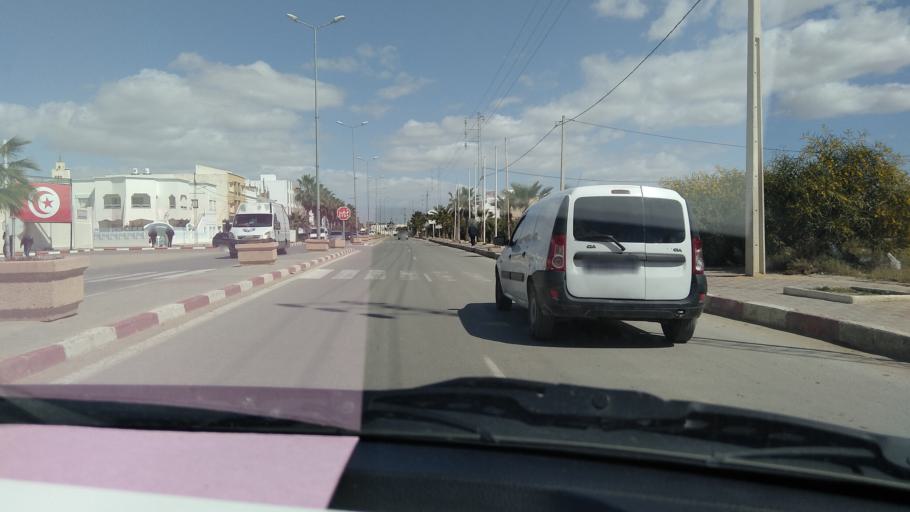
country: TN
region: Al Qayrawan
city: Kairouan
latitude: 35.6903
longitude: 10.1020
